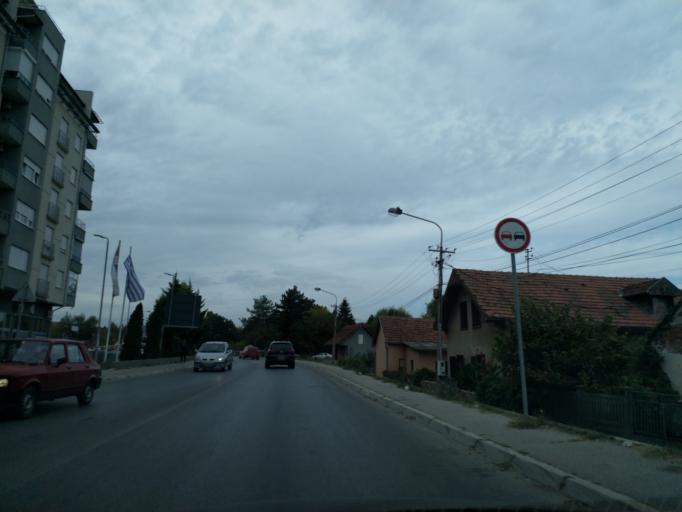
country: RS
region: Central Serbia
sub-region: Pomoravski Okrug
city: Jagodina
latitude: 43.9863
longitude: 21.2494
